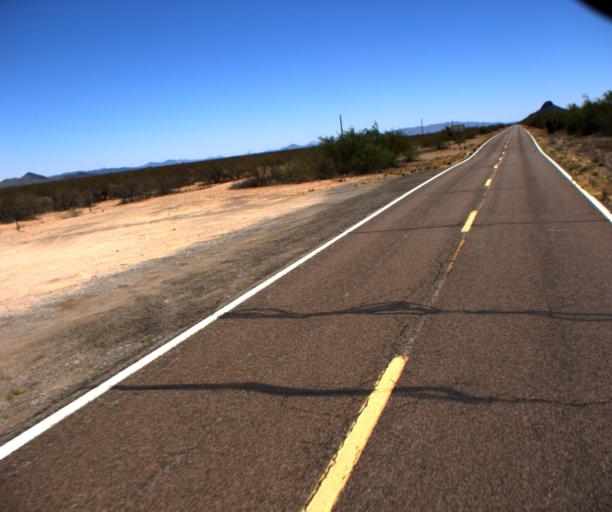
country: US
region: Arizona
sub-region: Pima County
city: Ajo
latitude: 32.2062
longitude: -112.5717
